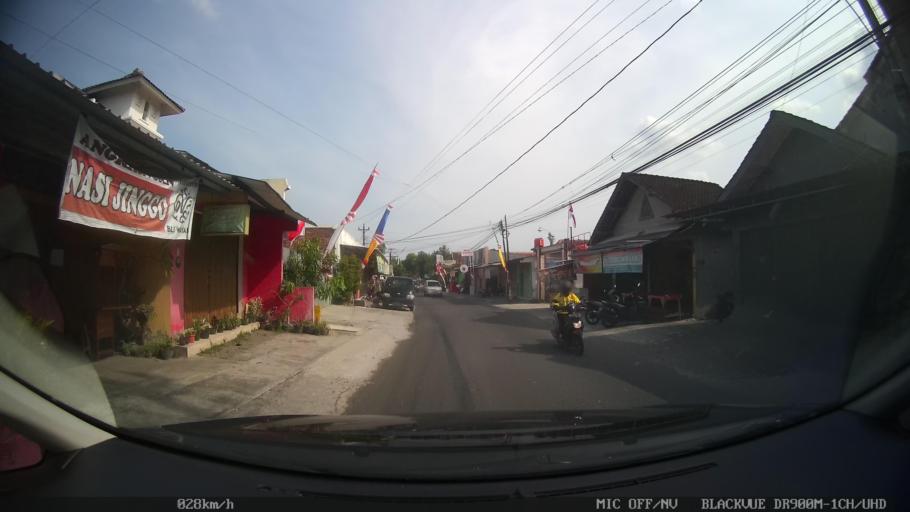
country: ID
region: Daerah Istimewa Yogyakarta
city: Depok
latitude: -7.7716
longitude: 110.4237
